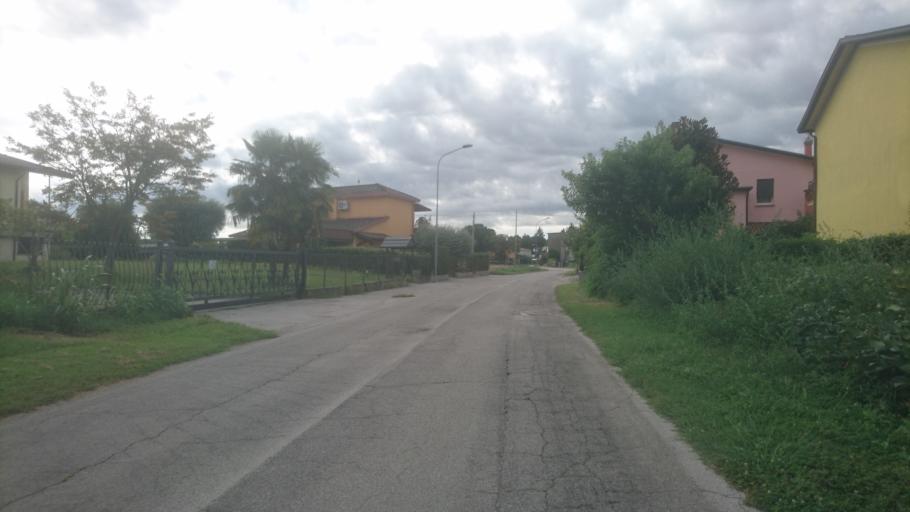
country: IT
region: Veneto
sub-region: Provincia di Venezia
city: Vigonovo
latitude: 45.3968
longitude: 11.9985
